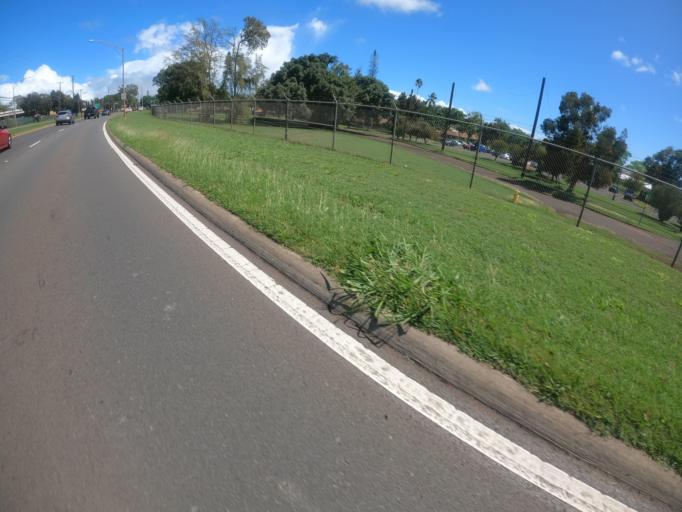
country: US
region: Hawaii
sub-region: Honolulu County
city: Schofield Barracks
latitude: 21.4840
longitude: -158.0465
